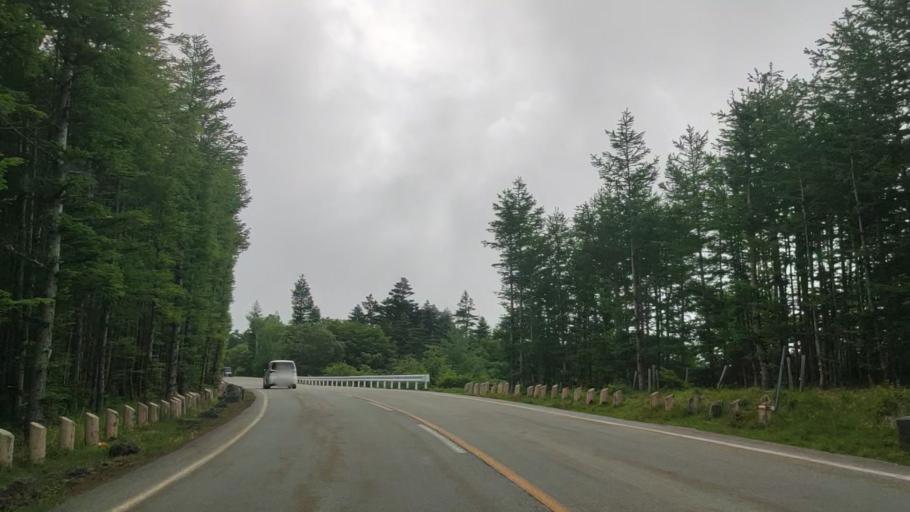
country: JP
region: Yamanashi
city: Fujikawaguchiko
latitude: 35.3880
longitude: 138.6905
